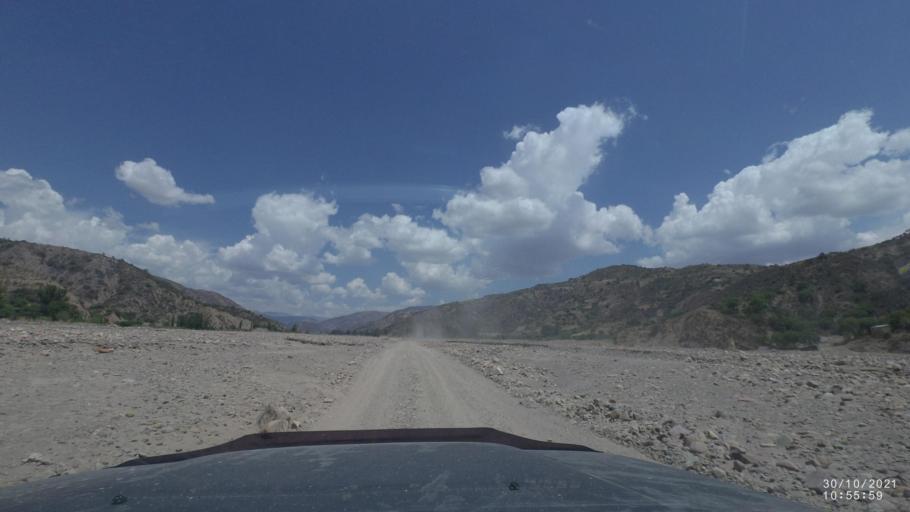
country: BO
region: Cochabamba
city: Sipe Sipe
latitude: -17.5404
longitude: -66.4924
